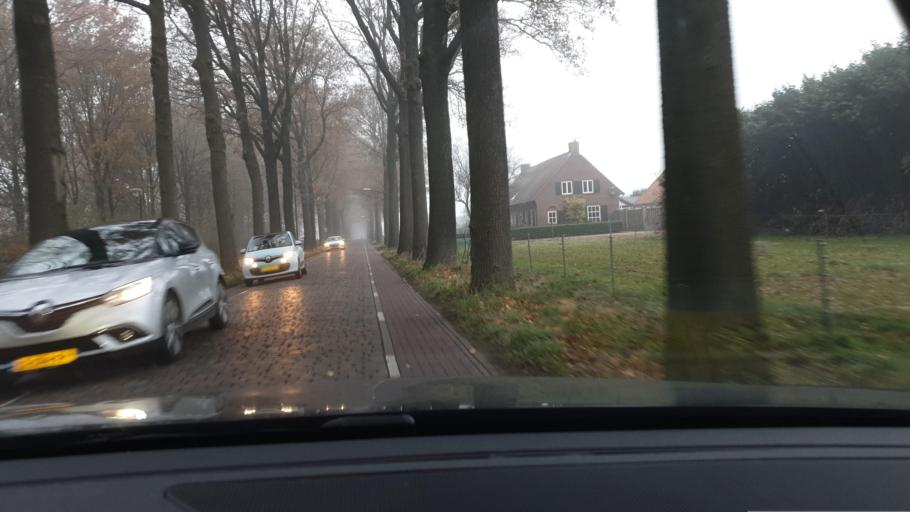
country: NL
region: North Brabant
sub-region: Gemeente Bladel en Netersel
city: Bladel
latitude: 51.3822
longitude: 5.2002
